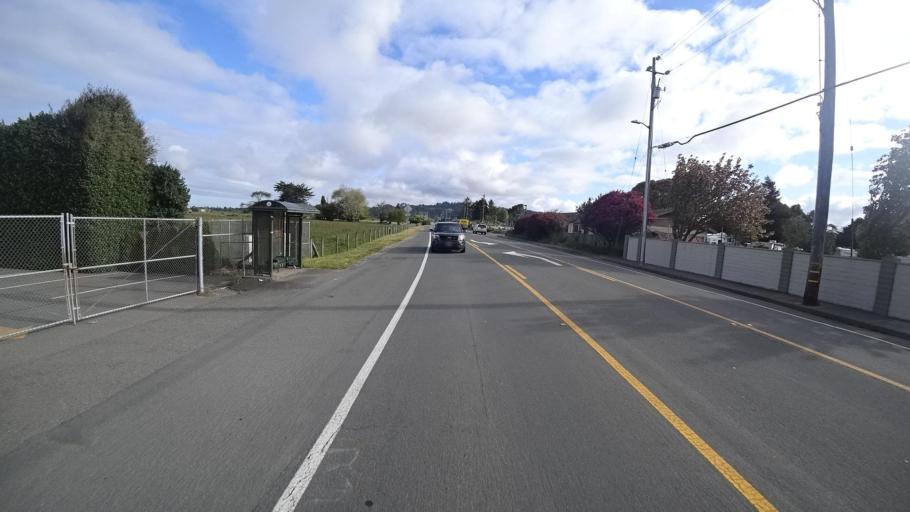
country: US
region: California
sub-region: Humboldt County
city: Arcata
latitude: 40.9012
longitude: -124.0914
